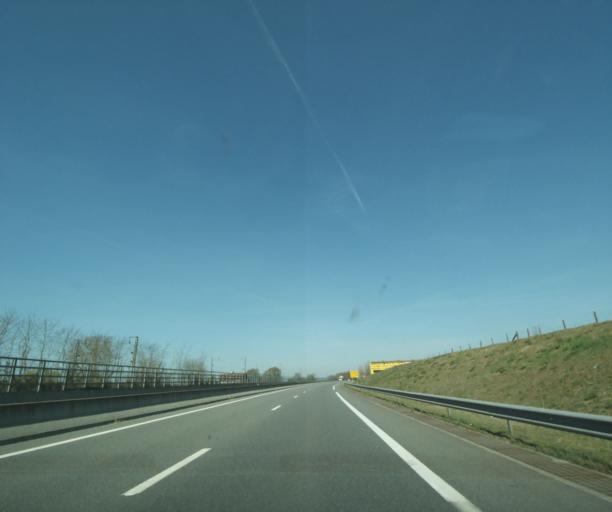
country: FR
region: Auvergne
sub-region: Departement de l'Allier
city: Trevol
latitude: 46.6105
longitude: 3.2928
